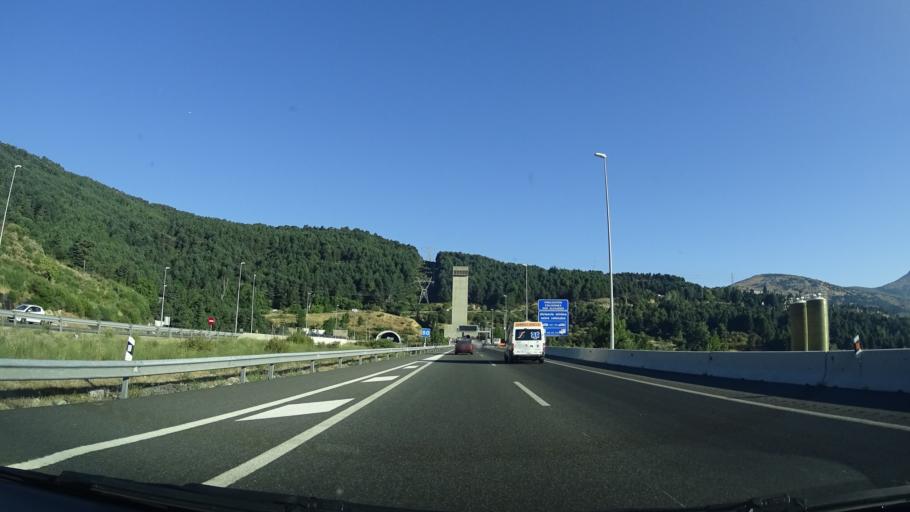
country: ES
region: Madrid
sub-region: Provincia de Madrid
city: Guadarrama
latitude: 40.6973
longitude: -4.1270
